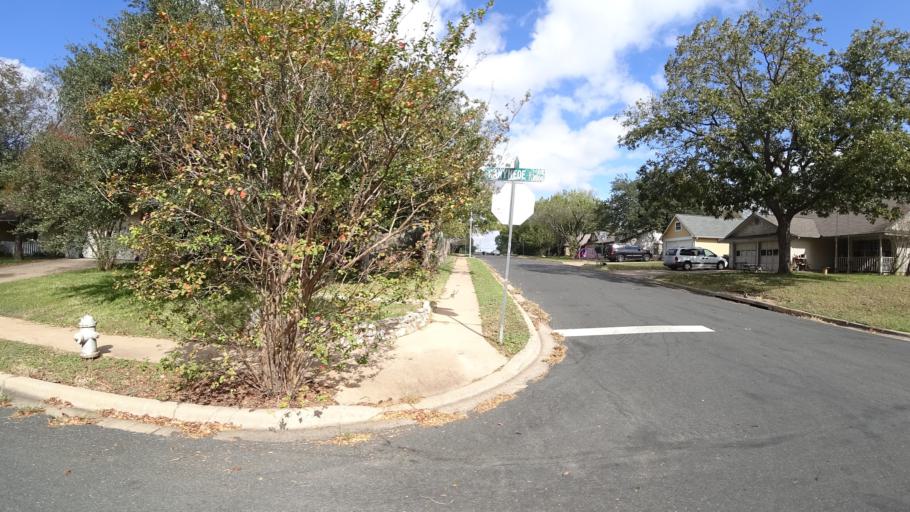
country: US
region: Texas
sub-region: Williamson County
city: Jollyville
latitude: 30.4289
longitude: -97.7270
